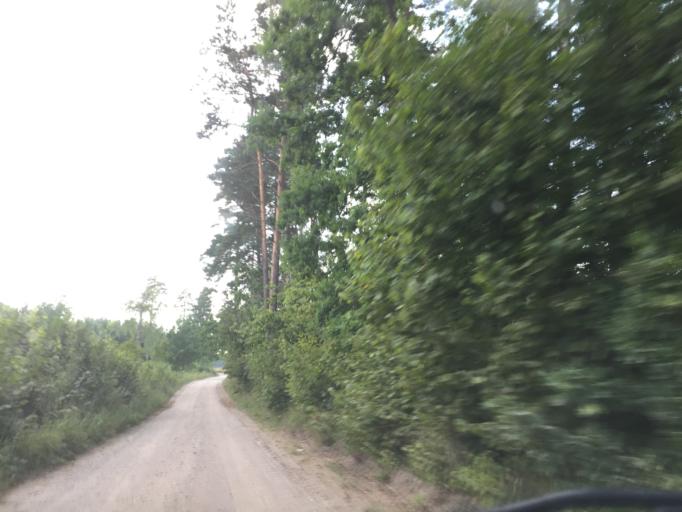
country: LT
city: Zagare
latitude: 56.4464
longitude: 23.1563
